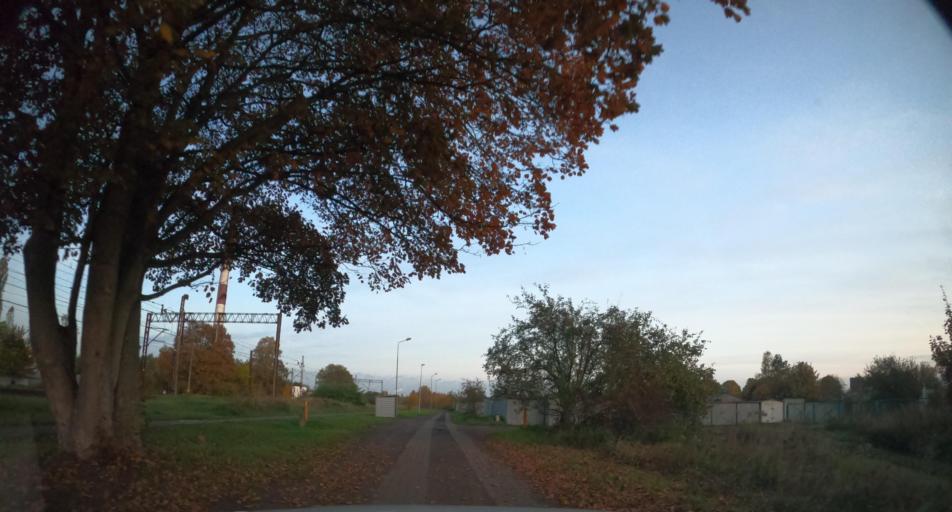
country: PL
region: West Pomeranian Voivodeship
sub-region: Powiat policki
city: Police
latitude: 53.5520
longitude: 14.5650
